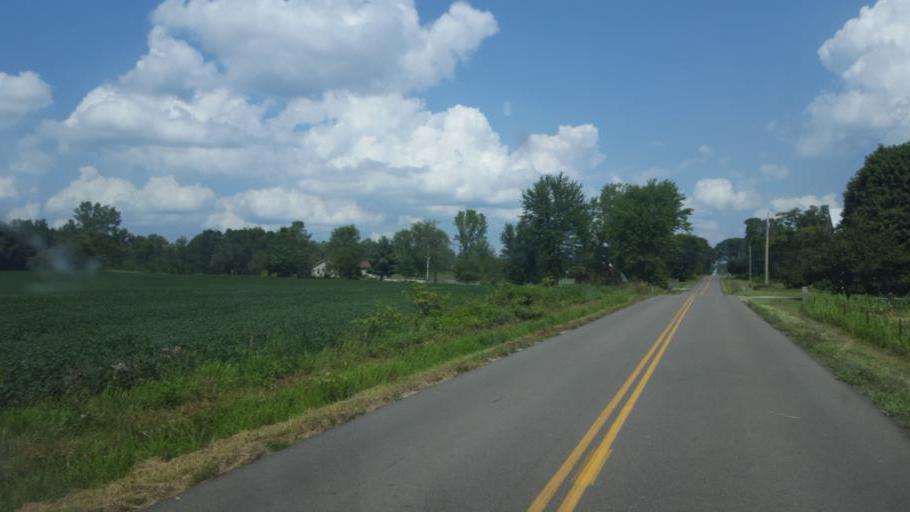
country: US
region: Ohio
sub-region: Knox County
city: Centerburg
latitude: 40.3242
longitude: -82.5807
